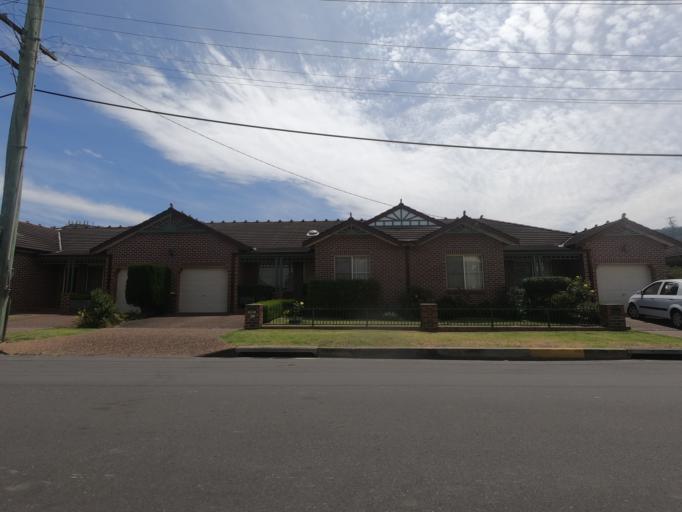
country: AU
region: New South Wales
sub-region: Wollongong
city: Mount Ousley
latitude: -34.3897
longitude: 150.8805
